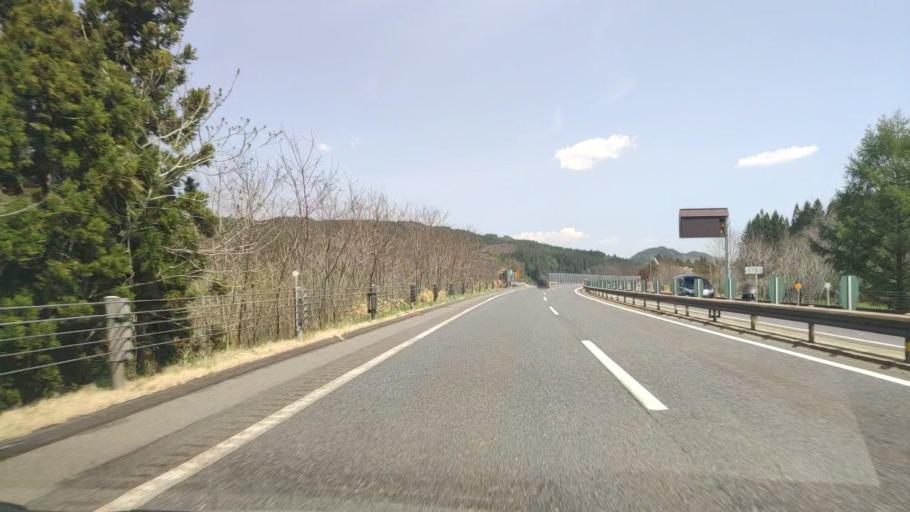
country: JP
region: Iwate
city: Ichinohe
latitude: 40.1967
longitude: 141.1775
